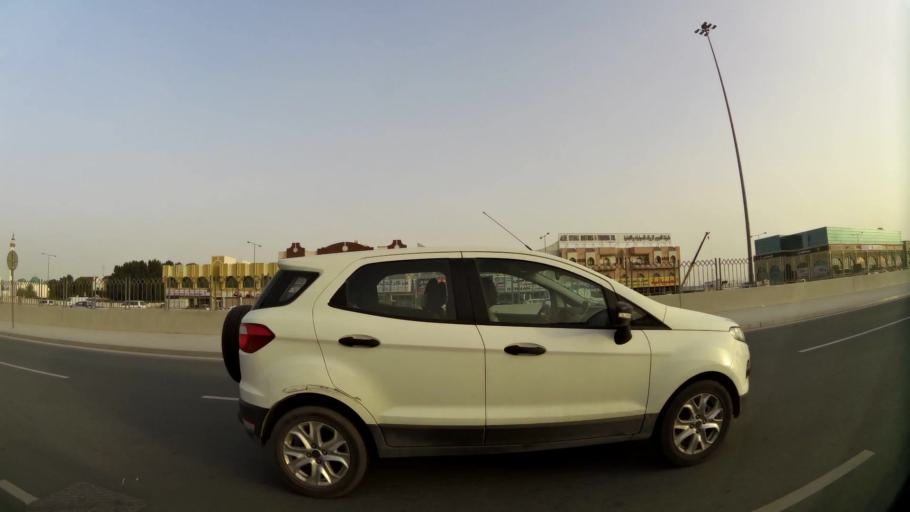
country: QA
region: Baladiyat ar Rayyan
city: Ar Rayyan
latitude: 25.2359
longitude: 51.4493
